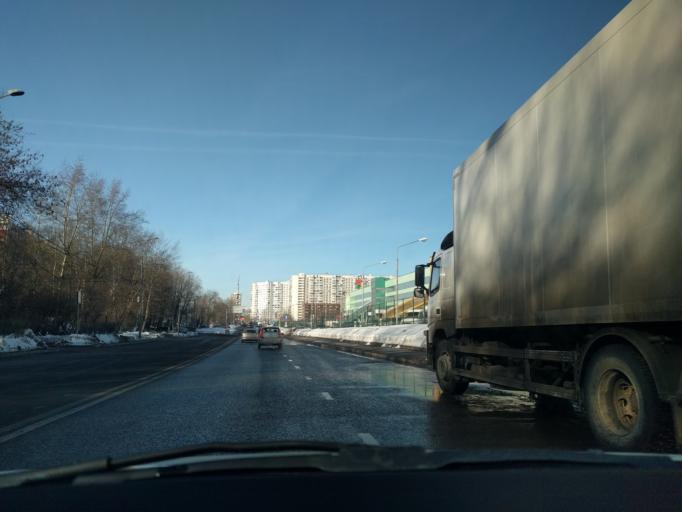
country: RU
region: Moscow
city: Gol'yanovo
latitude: 55.8096
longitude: 37.8296
